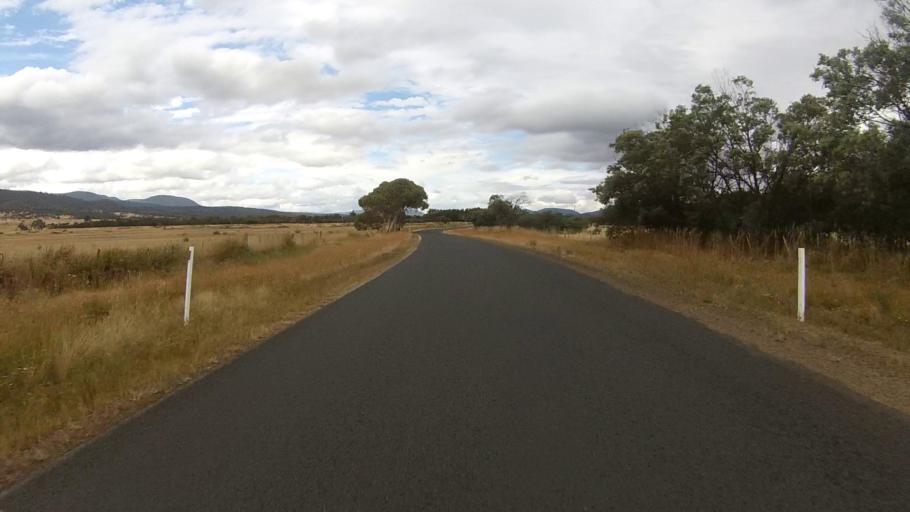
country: AU
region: Tasmania
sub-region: Northern Midlands
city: Evandale
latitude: -41.8238
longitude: 147.8236
